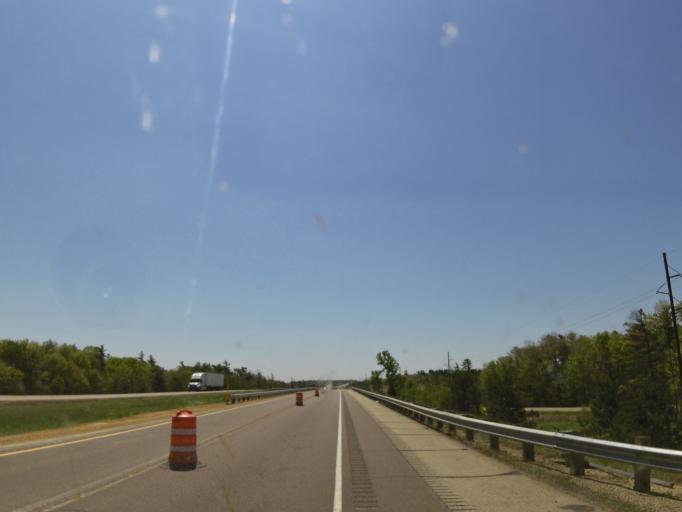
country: US
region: Wisconsin
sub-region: Monroe County
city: Tomah
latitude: 44.0725
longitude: -90.5224
